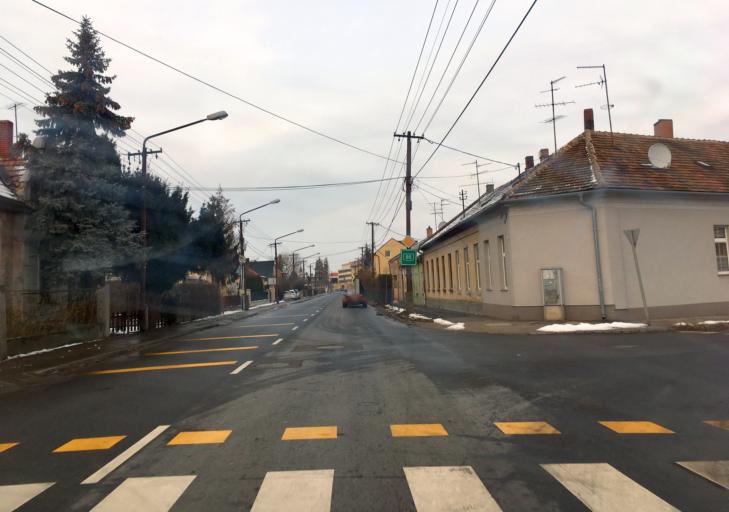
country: HU
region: Gyor-Moson-Sopron
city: Mosonmagyarovar
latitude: 47.8692
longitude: 17.2686
